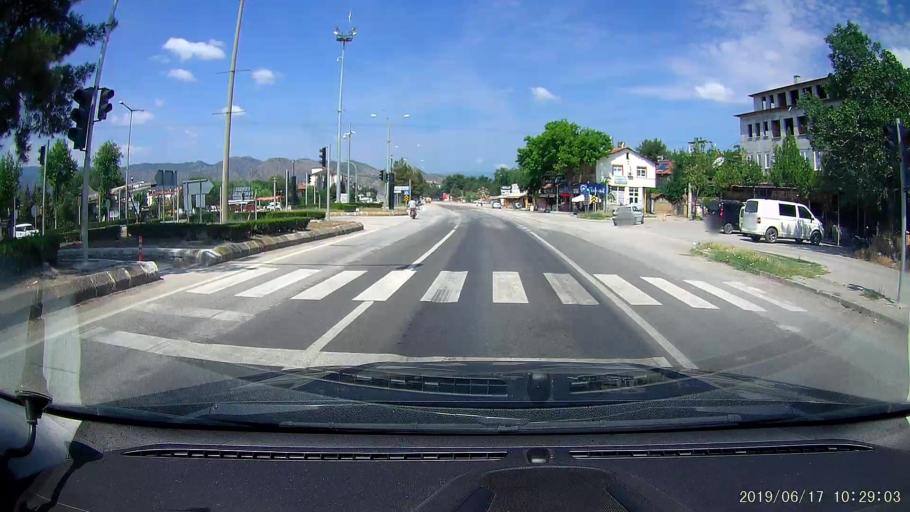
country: TR
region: Corum
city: Osmancik
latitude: 40.9798
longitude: 34.7993
